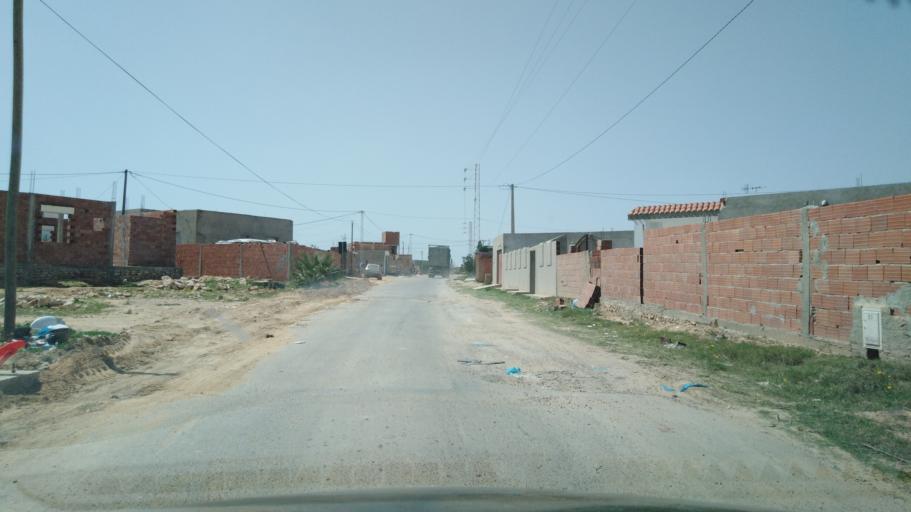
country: TN
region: Safaqis
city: Sfax
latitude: 34.7283
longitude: 10.5300
